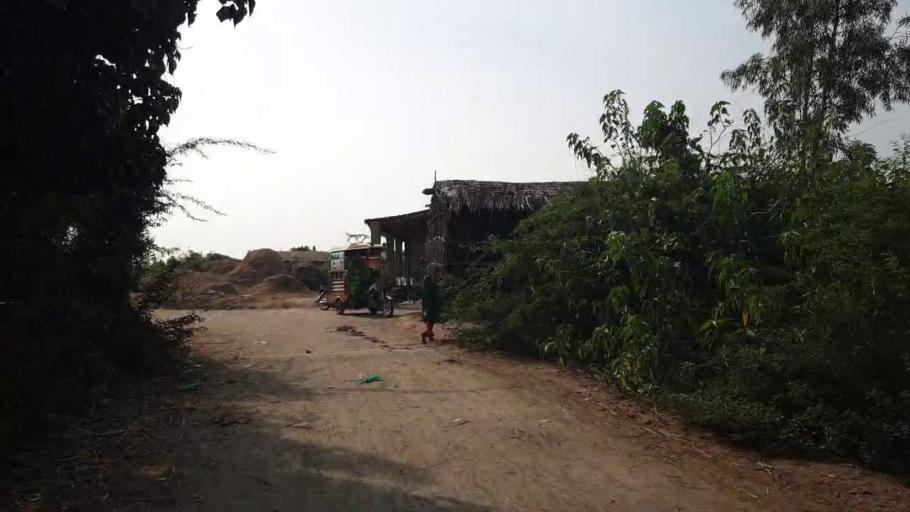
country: PK
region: Sindh
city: Rajo Khanani
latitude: 24.9126
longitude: 68.9196
